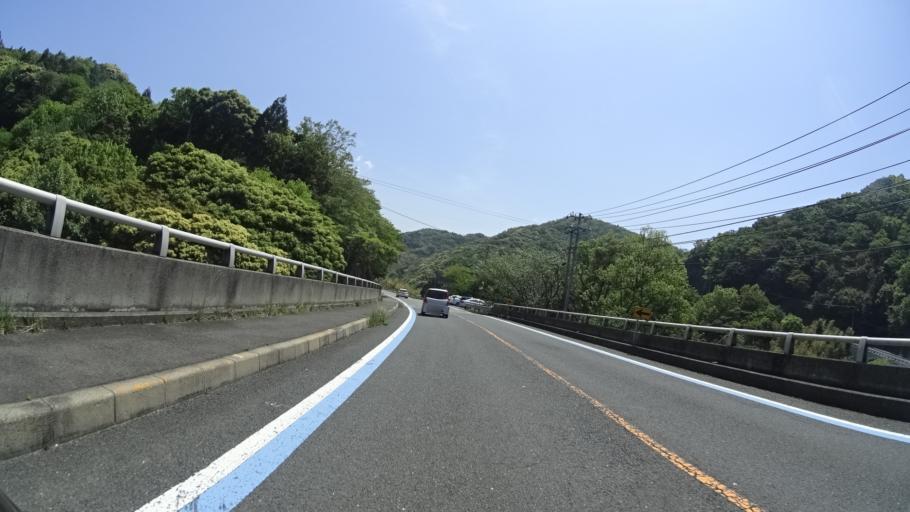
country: JP
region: Ehime
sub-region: Nishiuwa-gun
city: Ikata-cho
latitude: 33.4812
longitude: 132.3275
